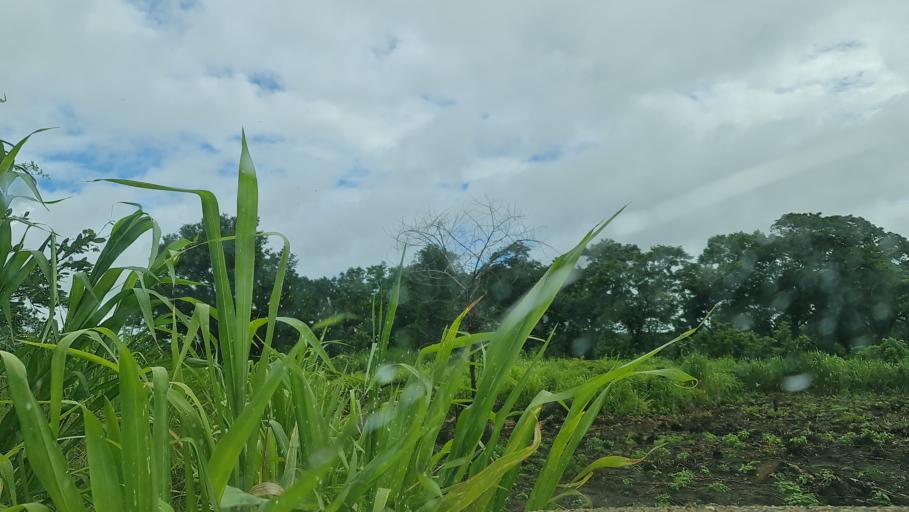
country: MW
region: Southern Region
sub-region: Nsanje District
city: Nsanje
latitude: -17.4474
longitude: 35.8420
